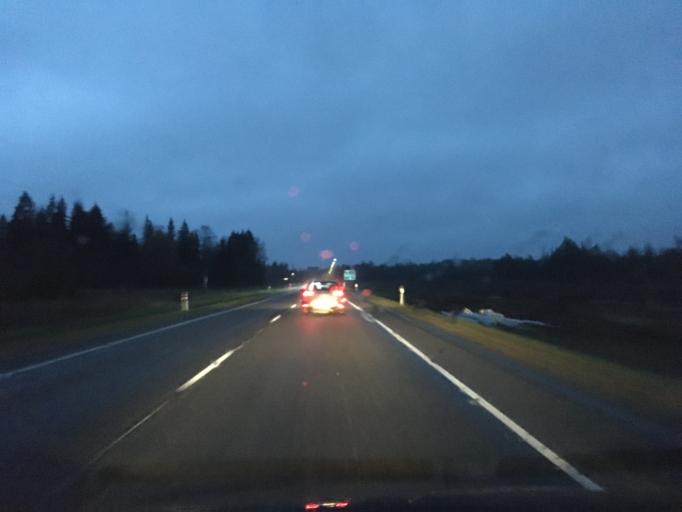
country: EE
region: Harju
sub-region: Nissi vald
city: Turba
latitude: 58.9888
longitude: 24.0582
